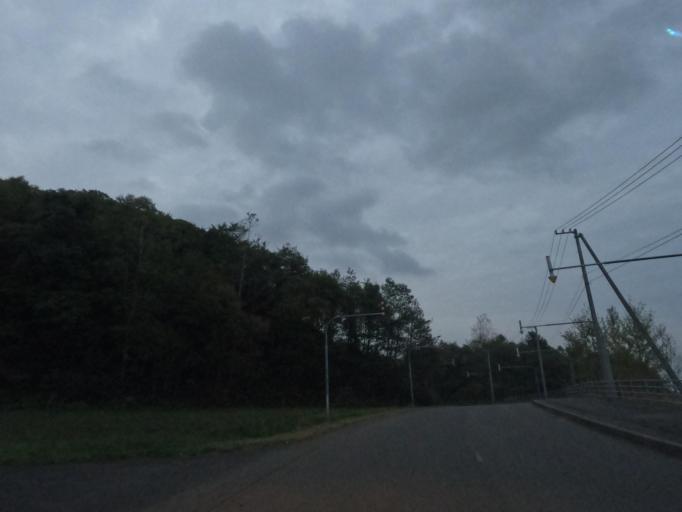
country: JP
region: Hokkaido
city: Date
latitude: 42.5600
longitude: 140.7903
